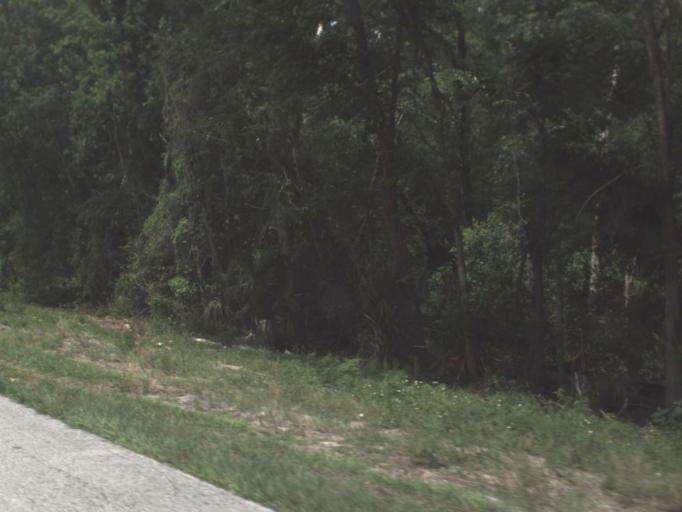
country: US
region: Florida
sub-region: Lake County
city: Lake Mack-Forest Hills
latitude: 29.0067
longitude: -81.3845
